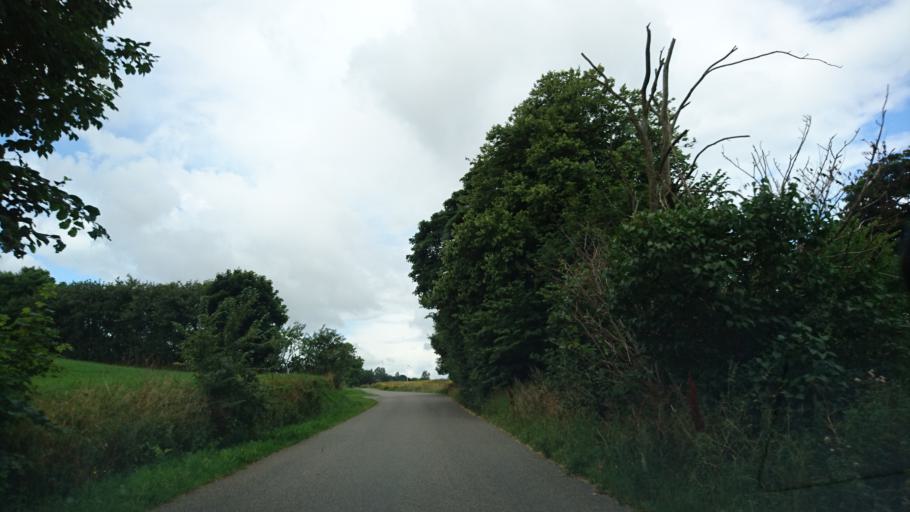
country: DK
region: North Denmark
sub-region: Hjorring Kommune
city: Tars
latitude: 57.3686
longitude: 10.2061
